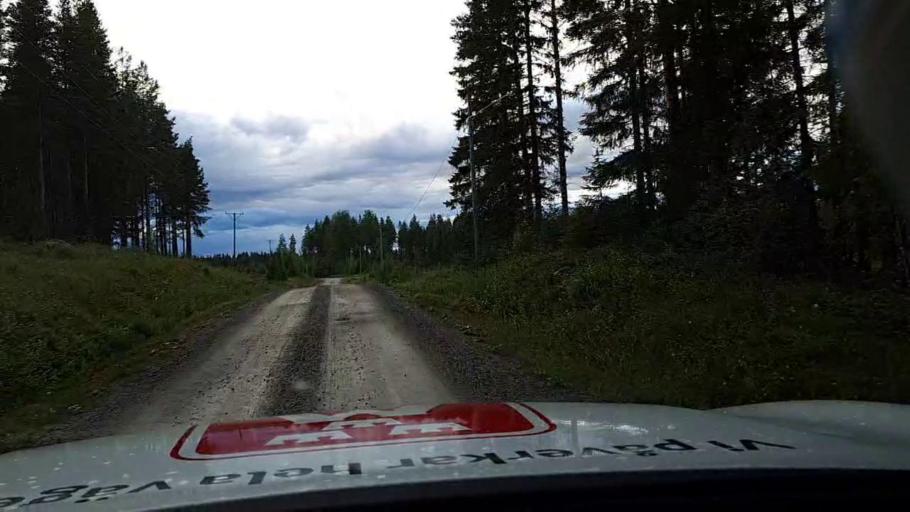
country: SE
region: Jaemtland
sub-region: Bergs Kommun
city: Hoverberg
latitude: 62.8812
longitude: 14.5954
